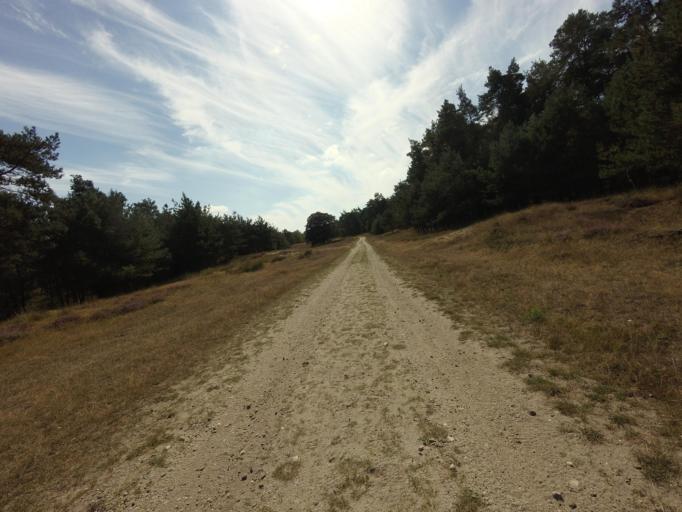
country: NL
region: Gelderland
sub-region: Gemeente Rheden
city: Rheden
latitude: 52.0423
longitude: 6.0061
